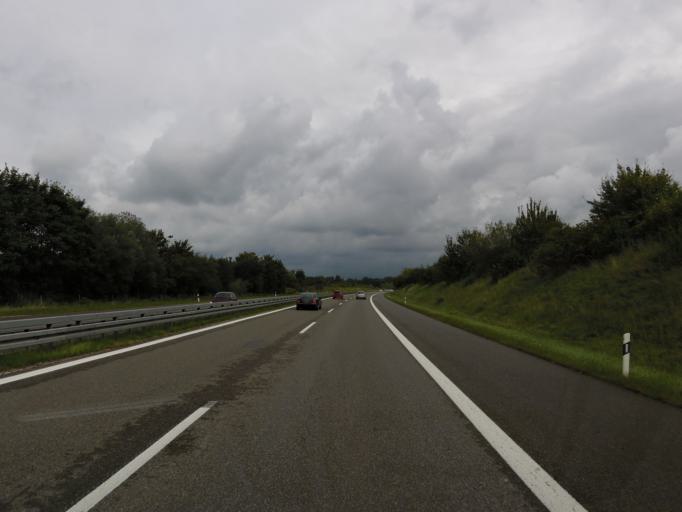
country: DE
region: Bavaria
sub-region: Swabia
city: Turkheim
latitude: 48.0403
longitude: 10.6331
